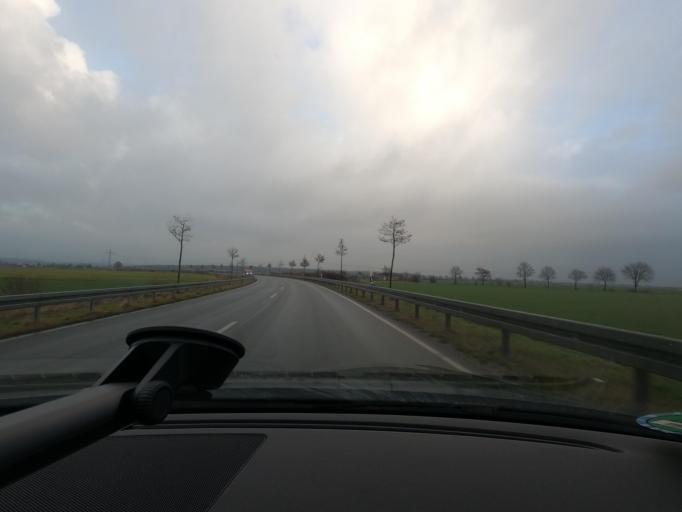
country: DE
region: North Rhine-Westphalia
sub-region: Regierungsbezirk Detmold
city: Buren
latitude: 51.5751
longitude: 8.5417
